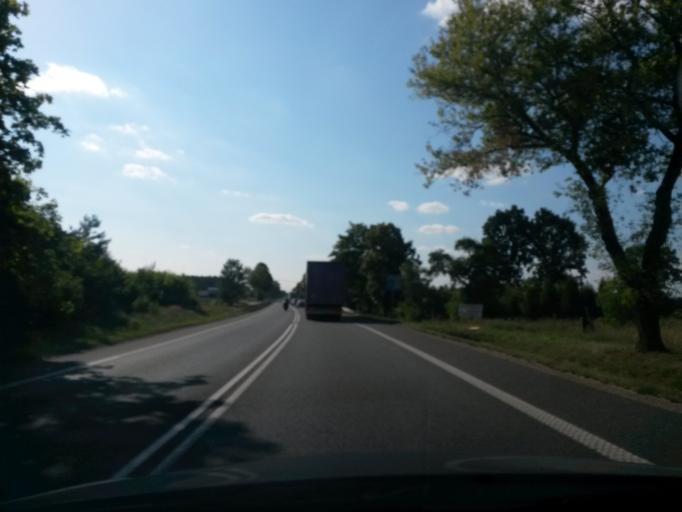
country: PL
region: Masovian Voivodeship
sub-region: Powiat sierpecki
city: Sierpc
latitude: 52.8504
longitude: 19.7047
